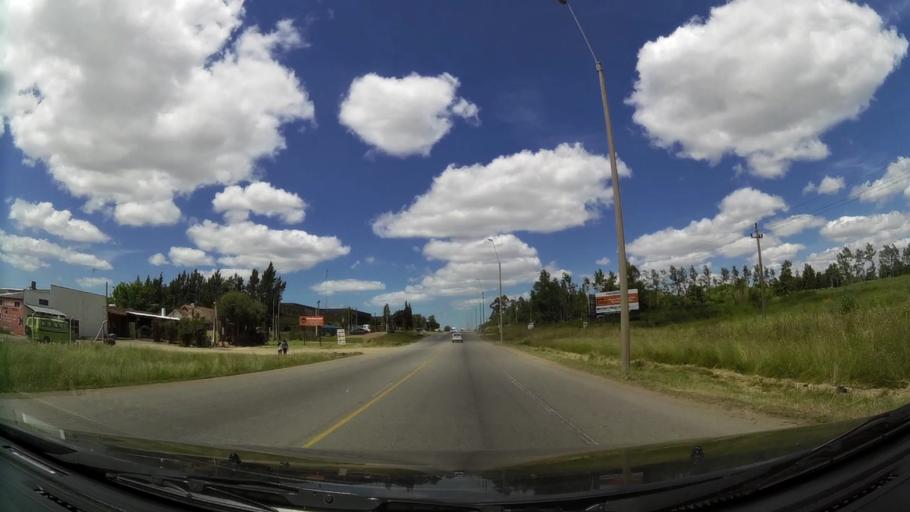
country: UY
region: Canelones
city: Colonia Nicolich
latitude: -34.7994
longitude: -56.0040
